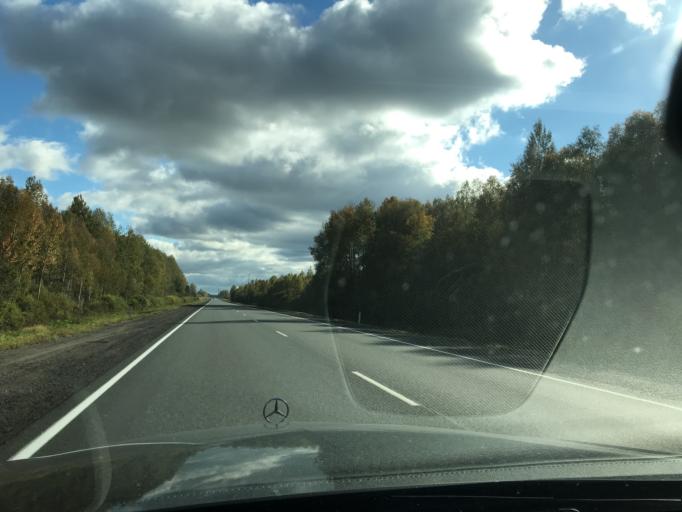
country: RU
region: Pskov
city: Pushkinskiye Gory
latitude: 57.0659
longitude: 28.5706
